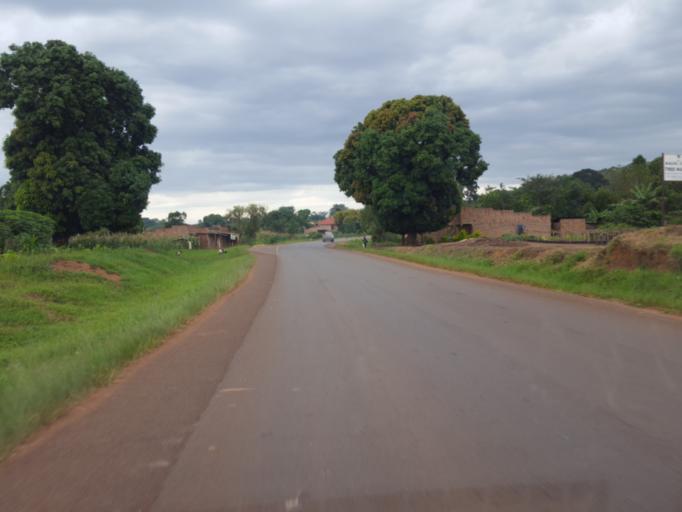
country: UG
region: Central Region
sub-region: Kiboga District
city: Kiboga
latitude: 0.8695
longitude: 31.8554
